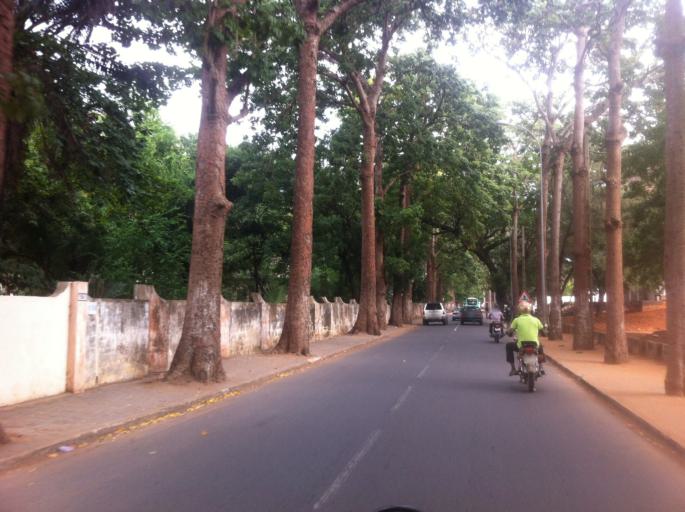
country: TG
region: Maritime
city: Lome
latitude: 6.1314
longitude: 1.2180
